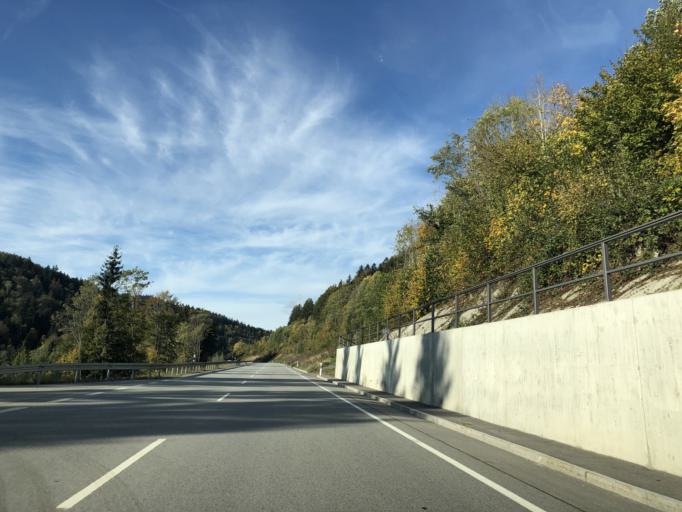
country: DE
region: Bavaria
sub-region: Lower Bavaria
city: Grafling
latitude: 48.9302
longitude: 12.9815
